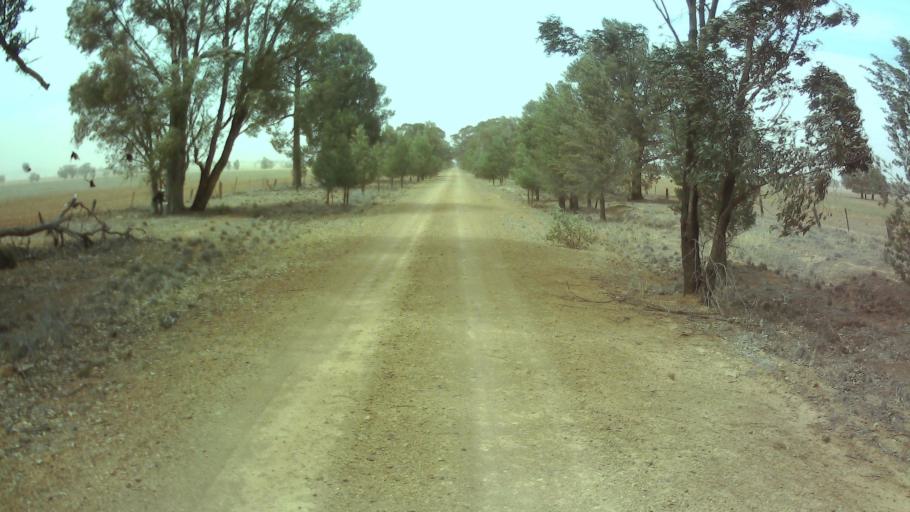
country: AU
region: New South Wales
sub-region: Weddin
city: Grenfell
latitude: -33.7208
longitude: 147.9648
